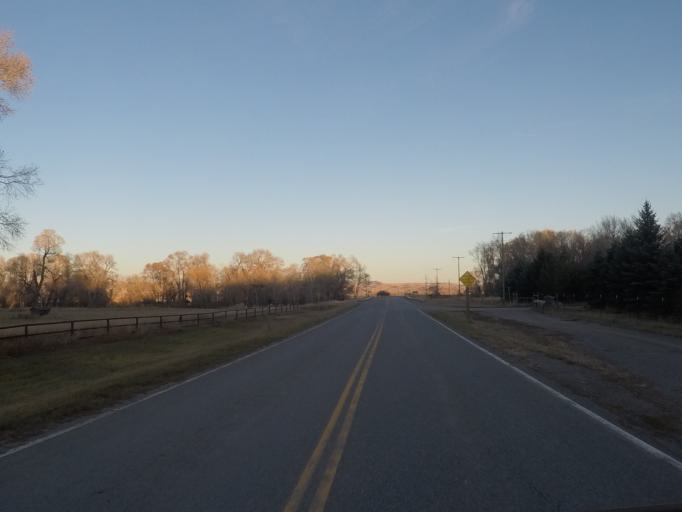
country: US
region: Montana
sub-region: Sweet Grass County
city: Big Timber
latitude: 45.7844
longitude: -109.8400
